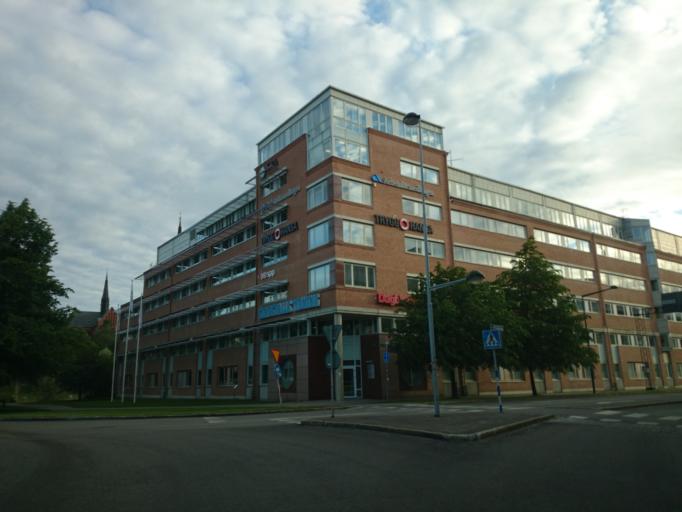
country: SE
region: Vaesternorrland
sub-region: Sundsvalls Kommun
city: Sundsvall
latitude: 62.3934
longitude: 17.3024
